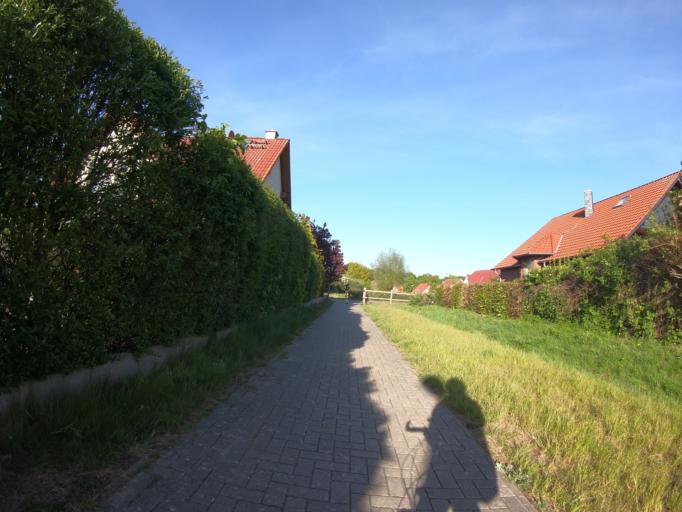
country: DE
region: Lower Saxony
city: Wagenhoff
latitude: 52.5241
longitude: 10.5279
